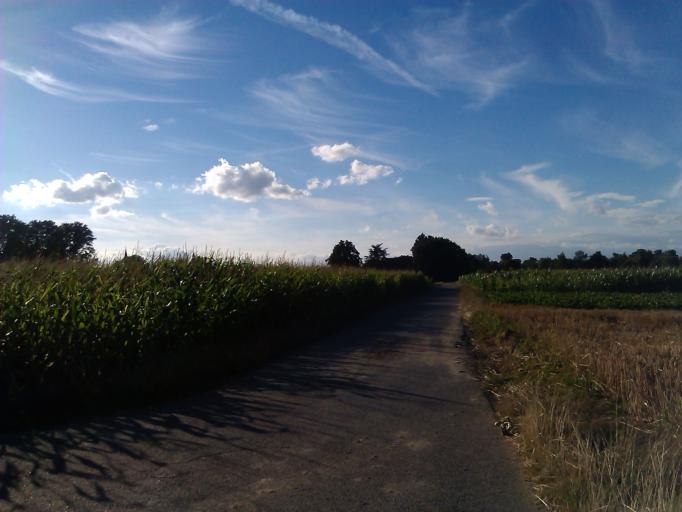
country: DE
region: Rheinland-Pfalz
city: Otterstadt
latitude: 49.3687
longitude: 8.4628
